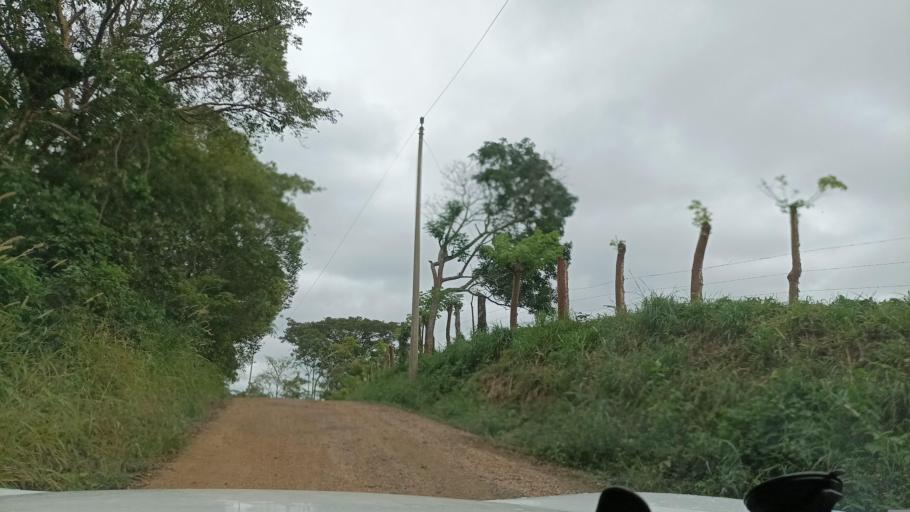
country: MX
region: Veracruz
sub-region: Moloacan
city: Cuichapa
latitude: 17.7961
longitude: -94.3774
